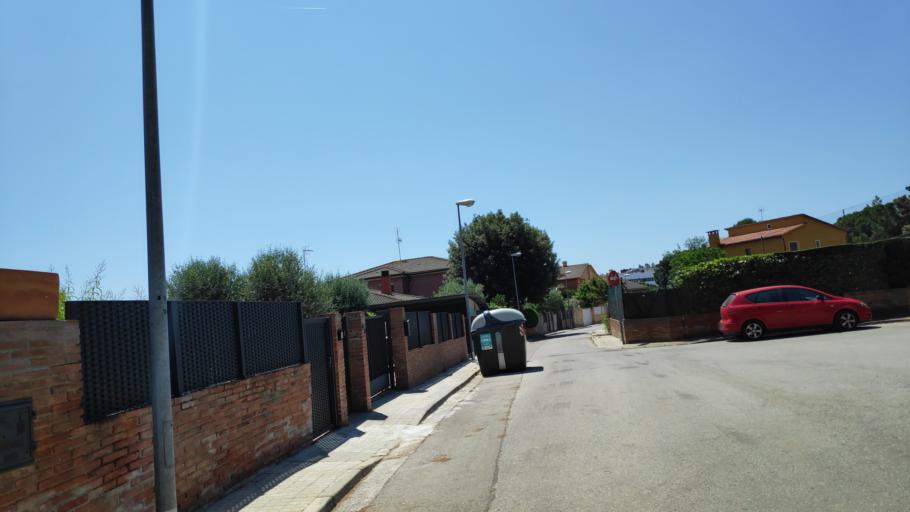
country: ES
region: Catalonia
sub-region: Provincia de Barcelona
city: Sant Quirze del Valles
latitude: 41.5584
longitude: 2.0763
